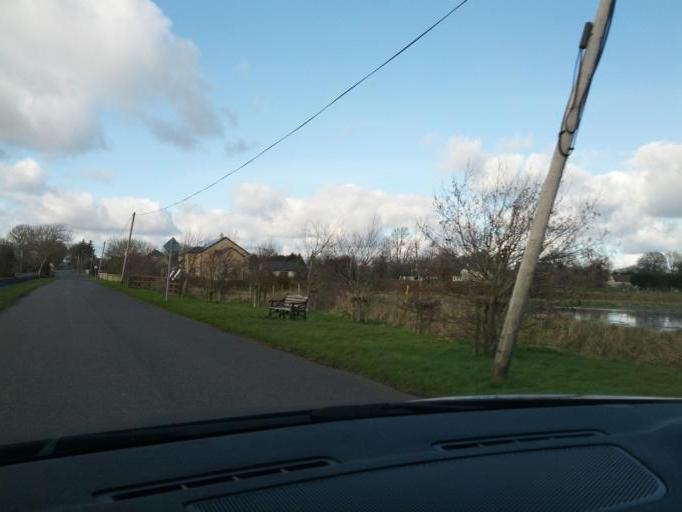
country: IE
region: Connaught
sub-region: County Galway
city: Athenry
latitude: 53.4786
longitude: -8.5698
